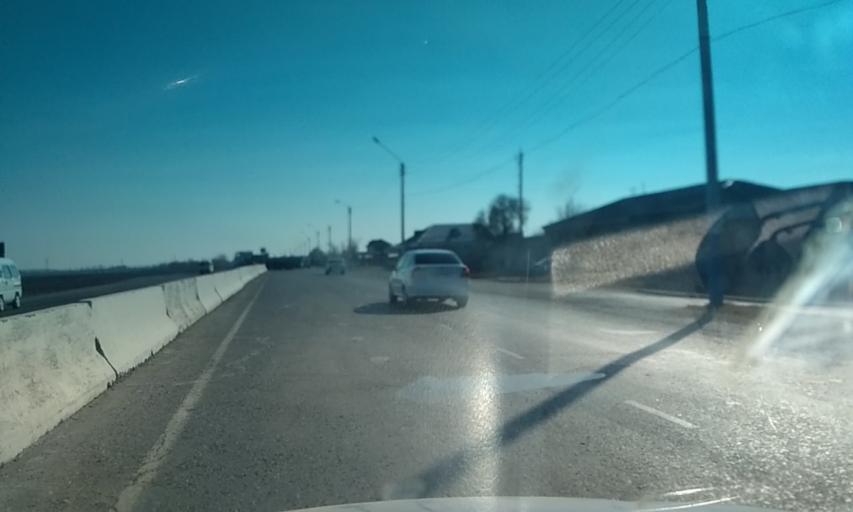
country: UZ
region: Sirdaryo
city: Guliston
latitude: 40.4663
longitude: 68.7720
